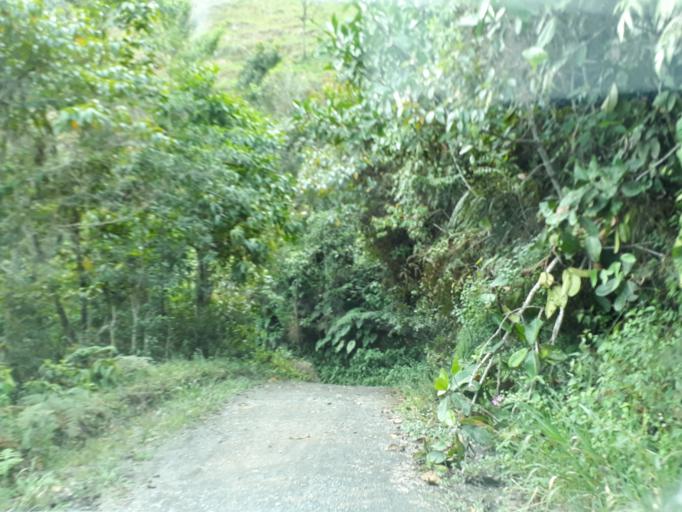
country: CO
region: Boyaca
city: Quipama
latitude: 5.3939
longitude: -74.1234
